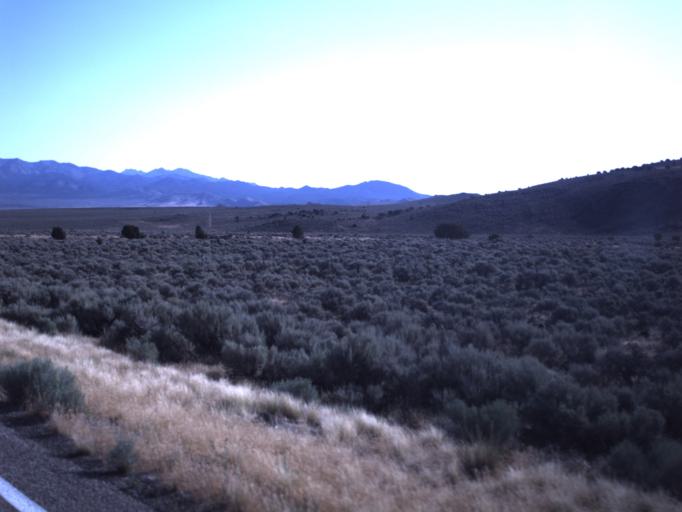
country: US
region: Utah
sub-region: Beaver County
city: Milford
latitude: 38.1462
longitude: -112.9598
